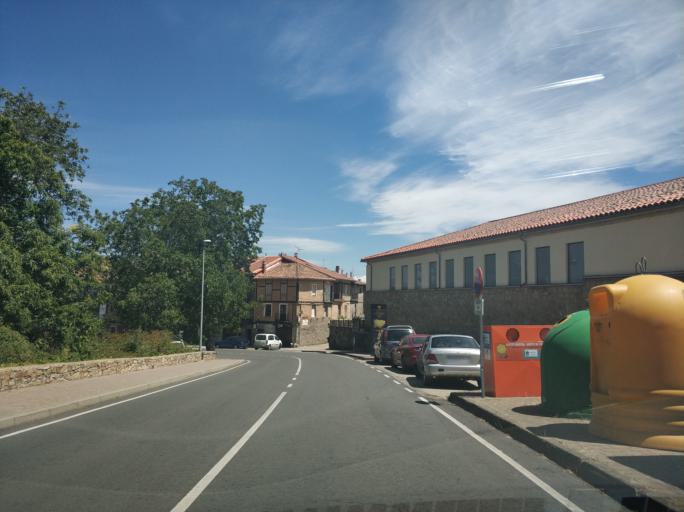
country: ES
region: Castille and Leon
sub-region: Provincia de Salamanca
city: La Alberca
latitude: 40.4897
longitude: -6.1127
